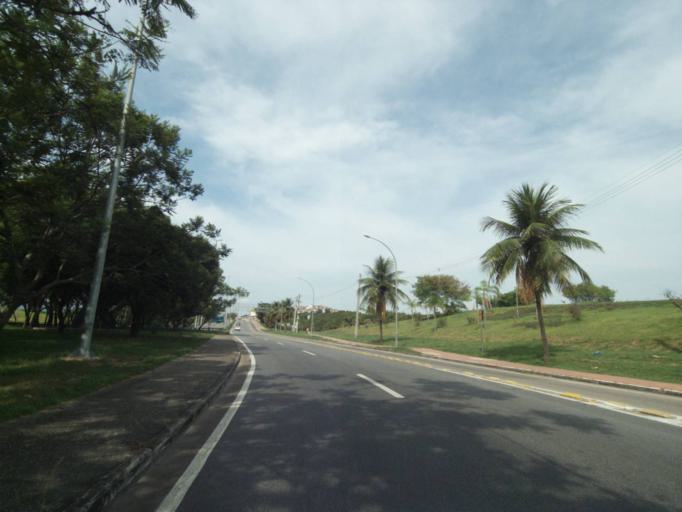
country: BR
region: Rio de Janeiro
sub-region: Rio De Janeiro
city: Rio de Janeiro
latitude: -22.8597
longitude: -43.2337
